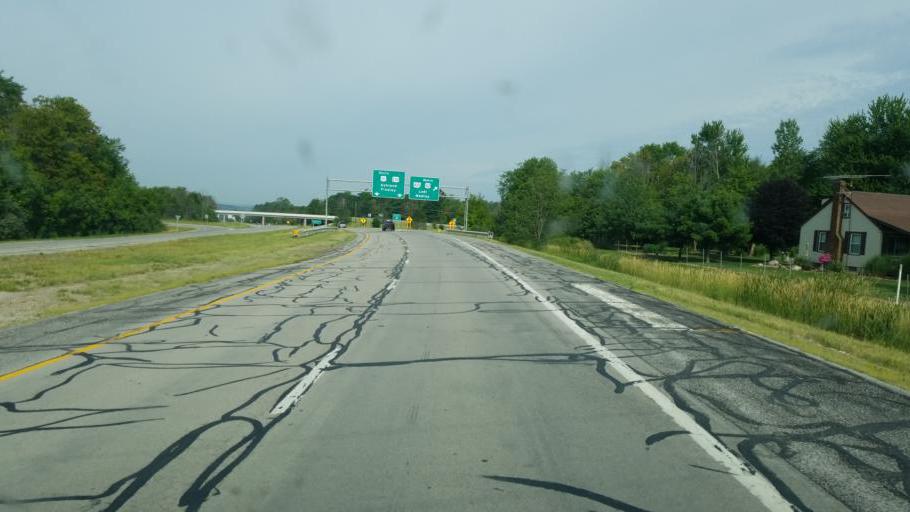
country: US
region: Ohio
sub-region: Medina County
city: Lodi
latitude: 41.0466
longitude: -81.9909
